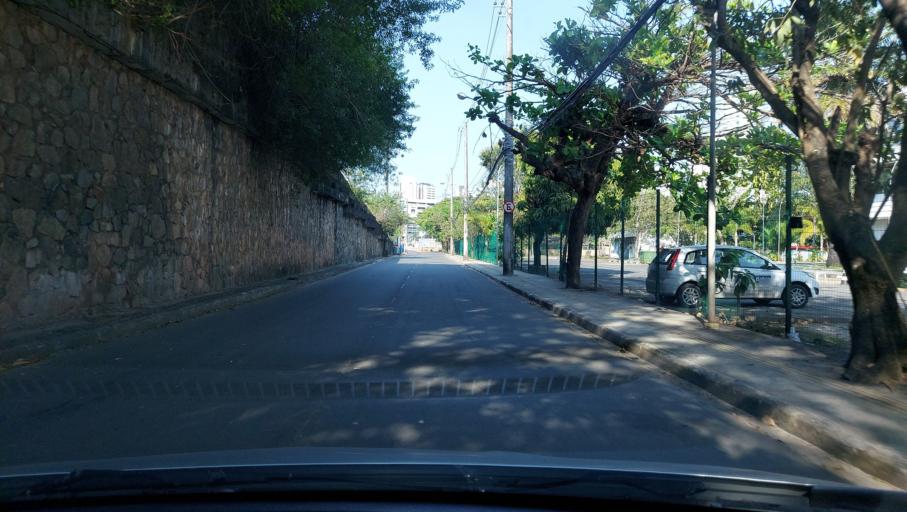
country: BR
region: Bahia
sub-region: Salvador
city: Salvador
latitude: -12.9834
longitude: -38.4688
